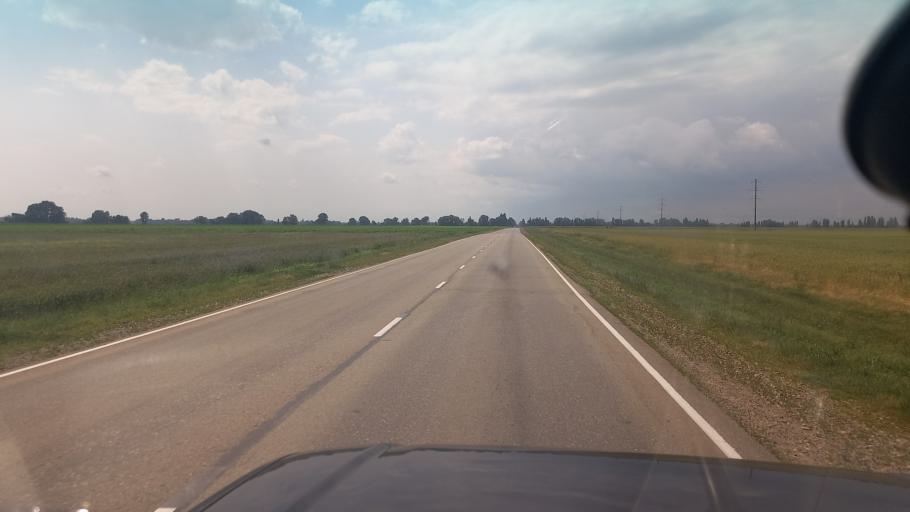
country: RU
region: Adygeya
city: Koshekhabl'
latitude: 44.9060
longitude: 40.4635
